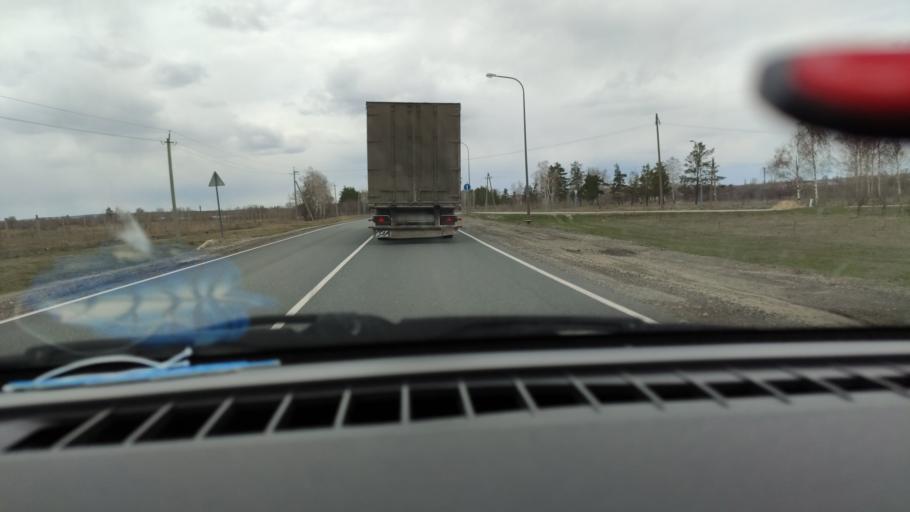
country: RU
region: Saratov
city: Sennoy
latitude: 52.1512
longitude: 46.9726
